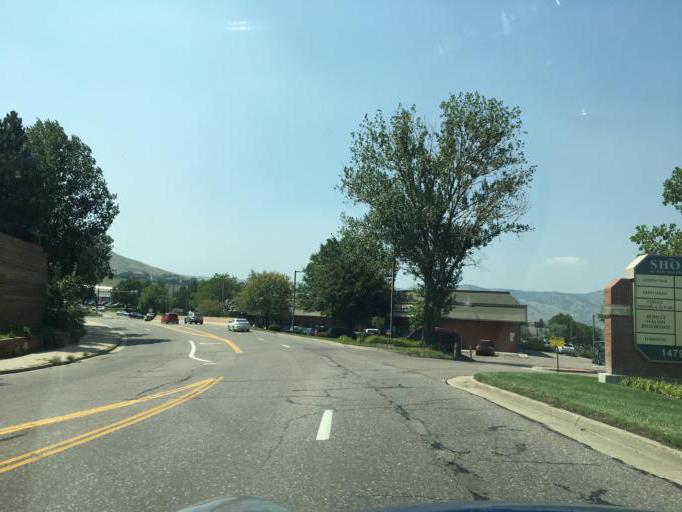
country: US
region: Colorado
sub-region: Jefferson County
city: West Pleasant View
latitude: 39.7246
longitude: -105.1636
